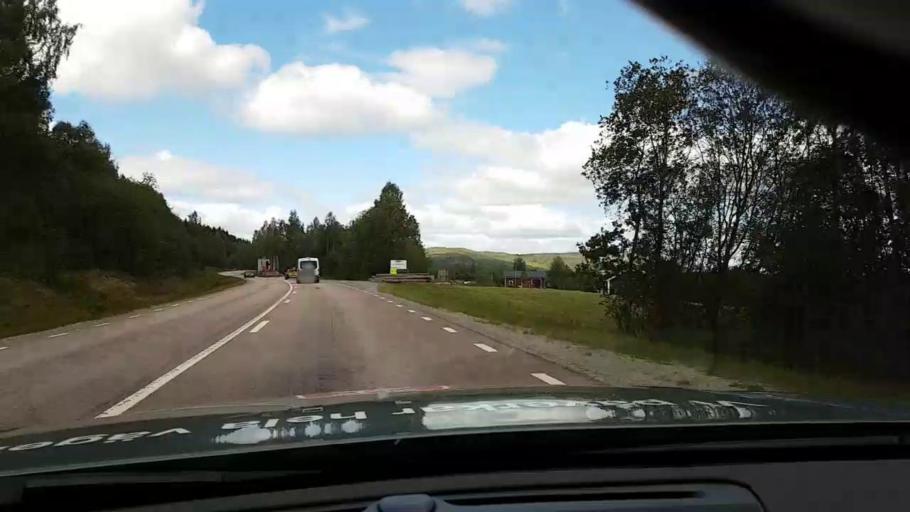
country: SE
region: Vaesternorrland
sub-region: OErnskoeldsviks Kommun
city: Bjasta
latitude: 63.3620
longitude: 18.4614
